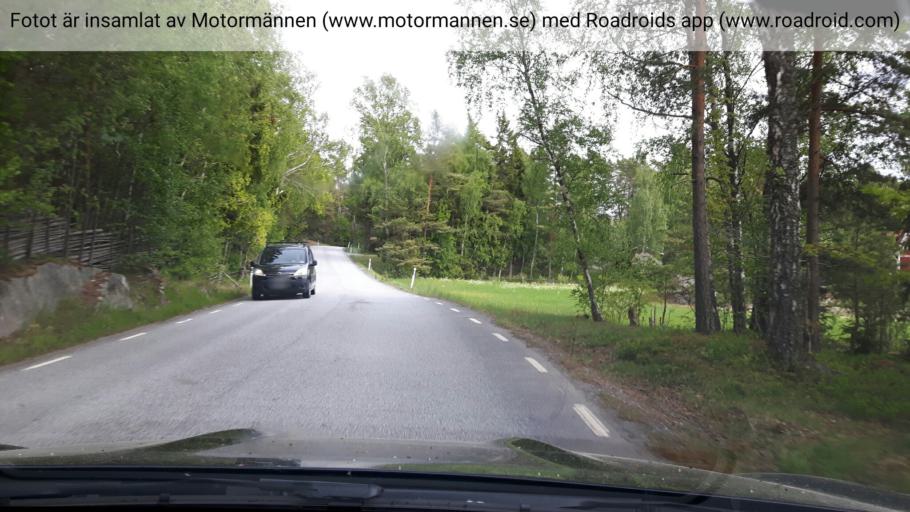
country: SE
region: Stockholm
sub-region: Norrtalje Kommun
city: Bjorko
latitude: 59.6669
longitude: 18.8513
